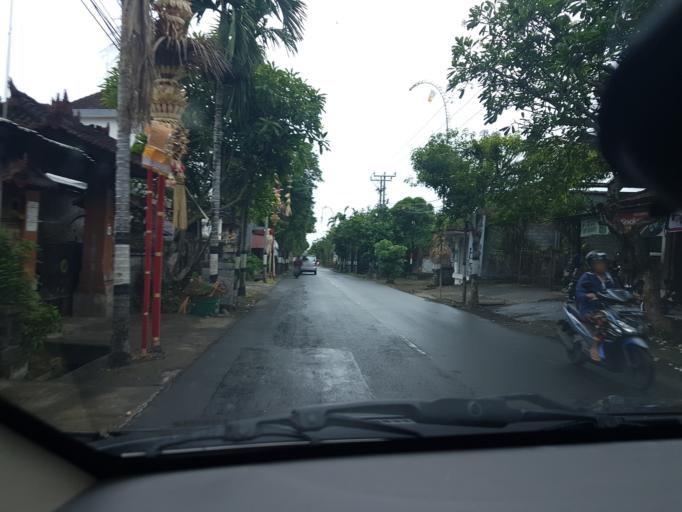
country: ID
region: Bali
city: Banjar Sedang
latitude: -8.5743
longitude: 115.2382
